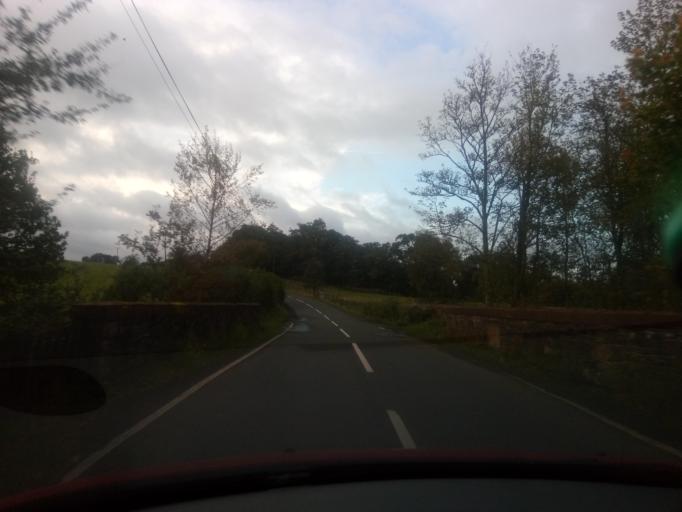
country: GB
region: Scotland
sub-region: The Scottish Borders
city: Jedburgh
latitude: 55.4201
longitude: -2.6308
